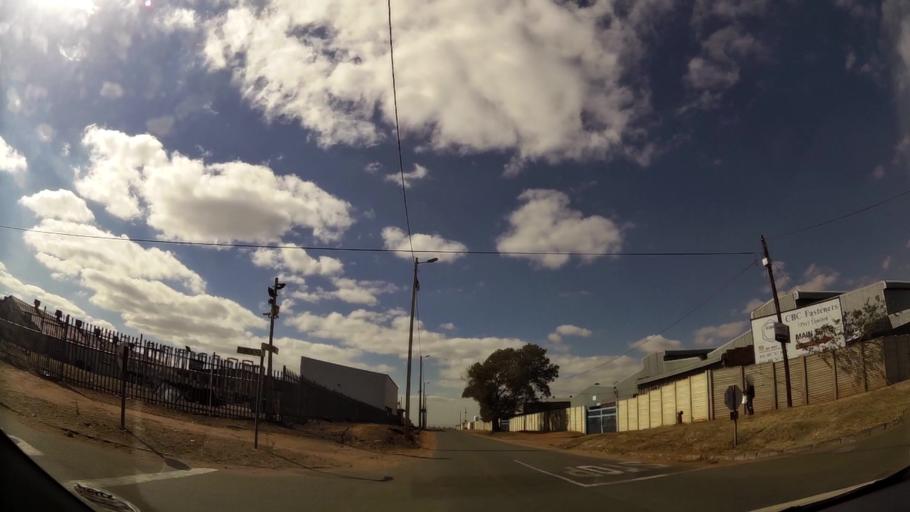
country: ZA
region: Gauteng
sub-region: West Rand District Municipality
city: Krugersdorp
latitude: -26.1172
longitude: 27.8129
